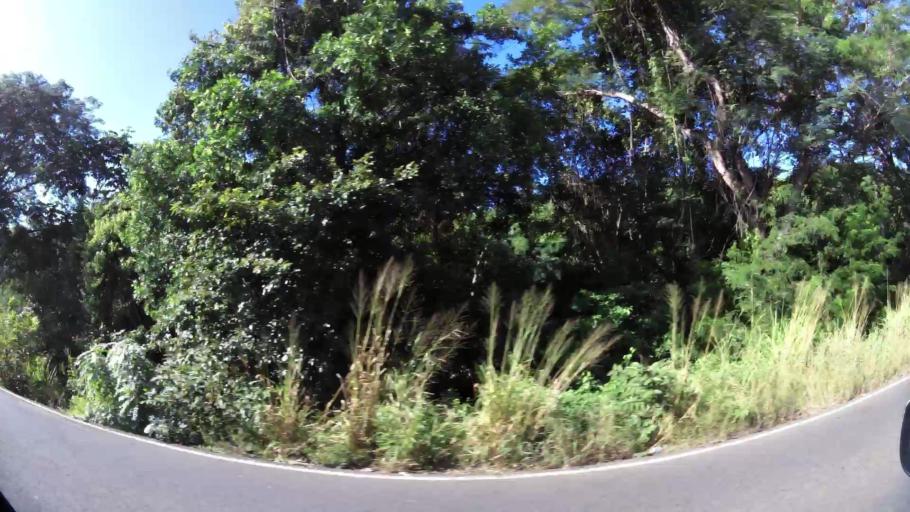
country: CR
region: Guanacaste
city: Belen
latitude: 10.3582
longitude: -85.7491
